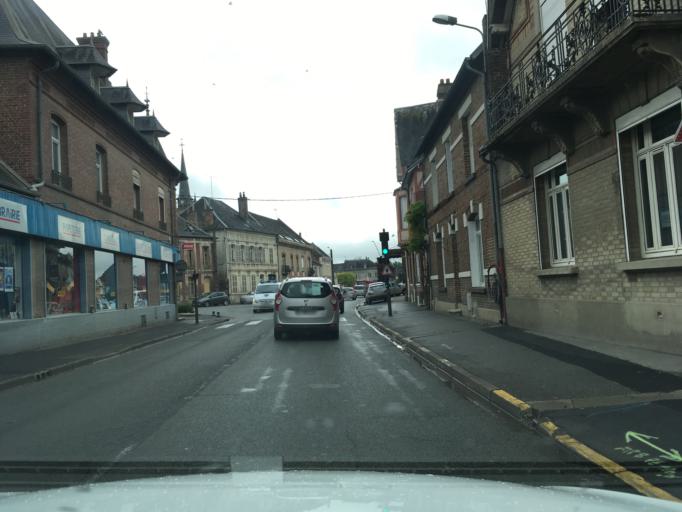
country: FR
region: Picardie
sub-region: Departement de l'Aisne
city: Origny-Sainte-Benoite
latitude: 49.8402
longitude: 3.4904
